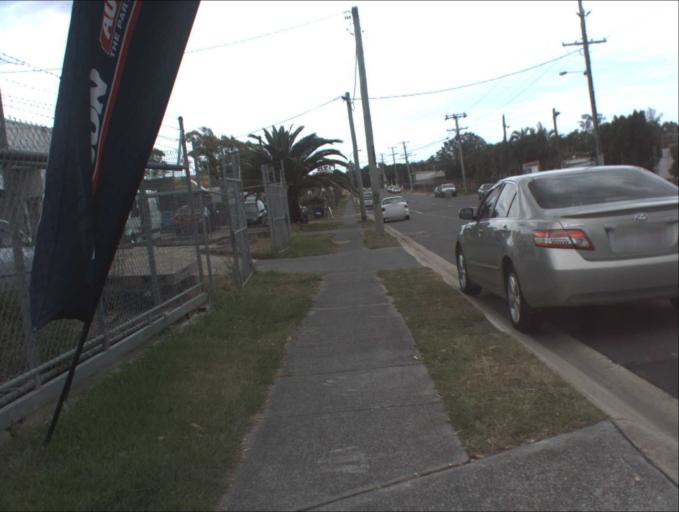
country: AU
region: Queensland
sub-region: Logan
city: Beenleigh
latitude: -27.7131
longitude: 153.1881
